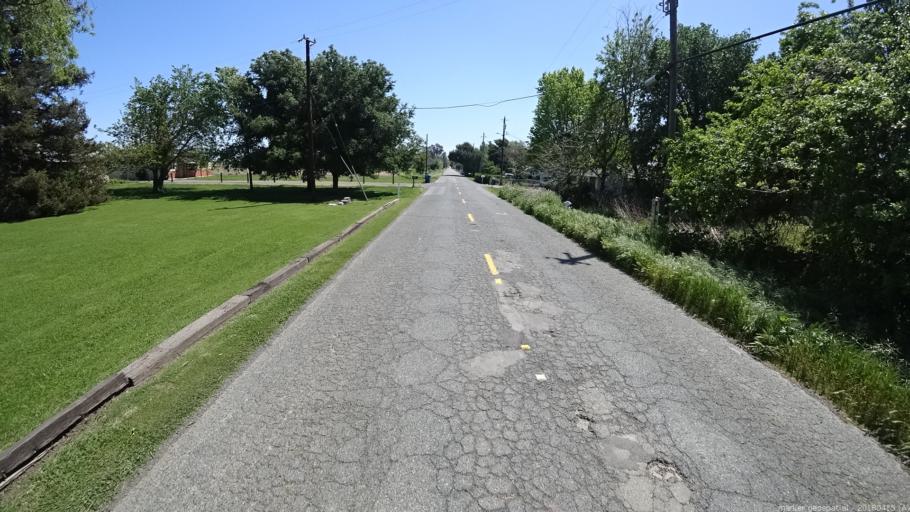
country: US
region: California
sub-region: Solano County
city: Rio Vista
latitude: 38.1664
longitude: -121.5949
